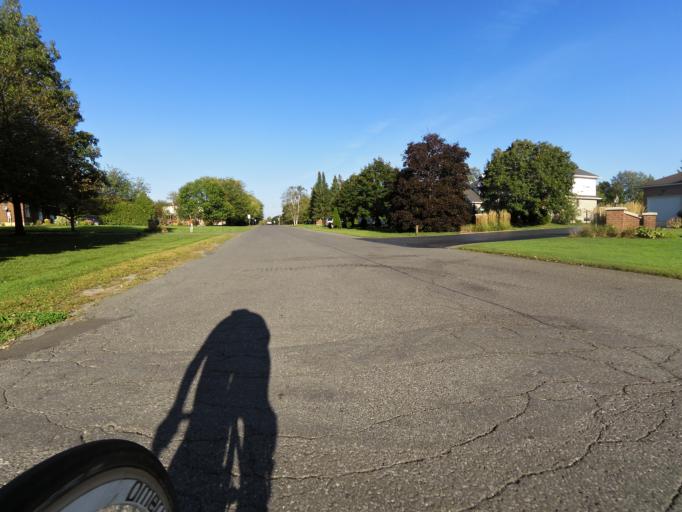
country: CA
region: Ontario
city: Bells Corners
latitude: 45.2191
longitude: -75.6847
